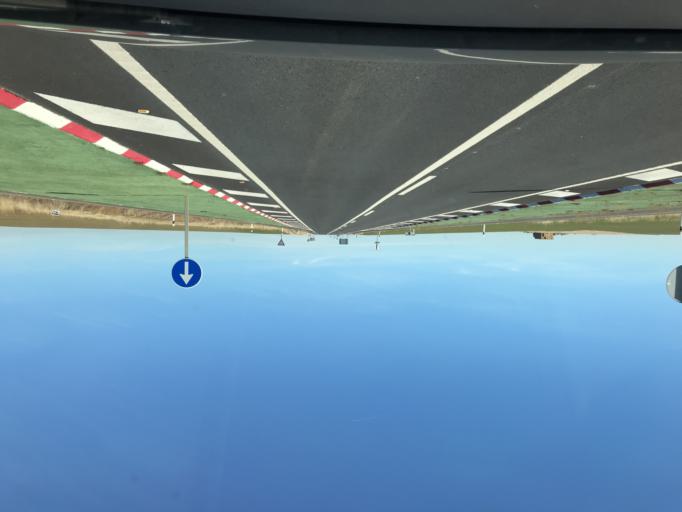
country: ES
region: Extremadura
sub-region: Provincia de Badajoz
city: Granja de Torrehermosa
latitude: 38.2980
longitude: -5.5577
